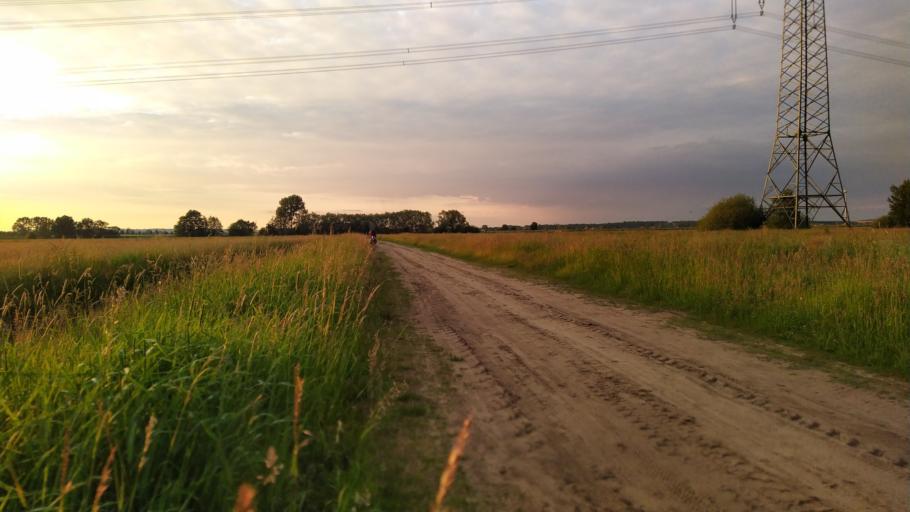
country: DE
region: Lower Saxony
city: Neu Wulmstorf
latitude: 53.4919
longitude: 9.8266
